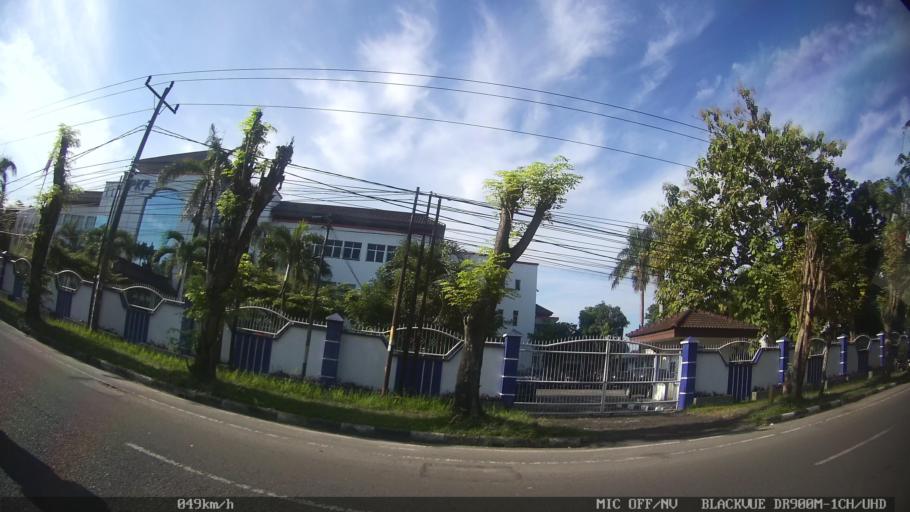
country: ID
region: North Sumatra
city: Sunggal
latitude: 3.5910
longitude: 98.6370
